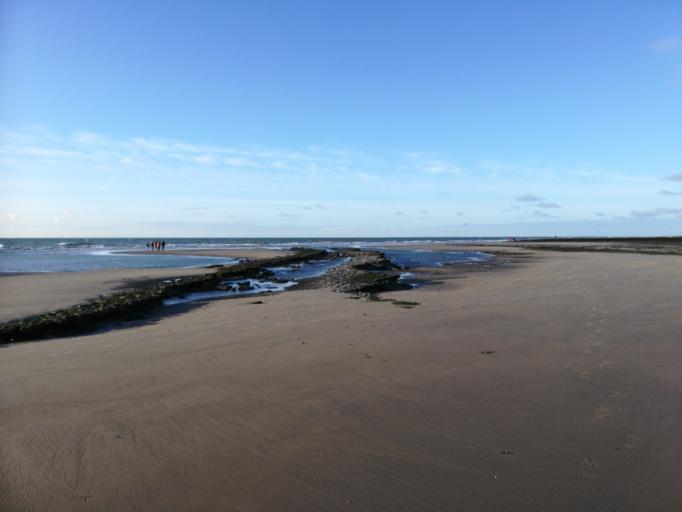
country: FR
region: Nord-Pas-de-Calais
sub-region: Departement du Pas-de-Calais
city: Ambleteuse
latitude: 50.8094
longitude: 1.5963
